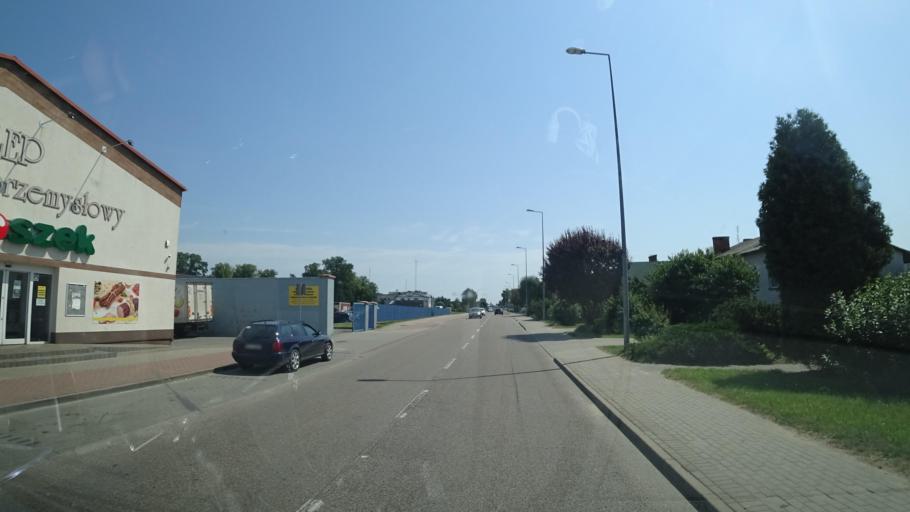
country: PL
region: Pomeranian Voivodeship
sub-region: Powiat chojnicki
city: Brusy
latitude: 53.8837
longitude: 17.7130
